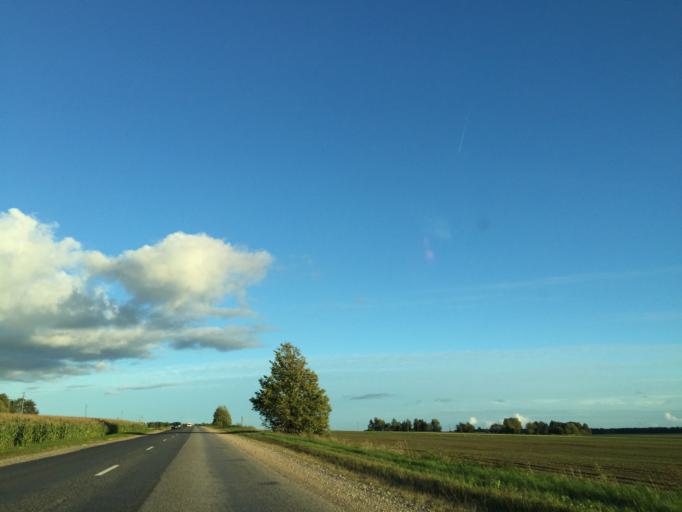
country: LV
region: Saldus Rajons
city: Saldus
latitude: 56.7082
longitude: 22.4198
